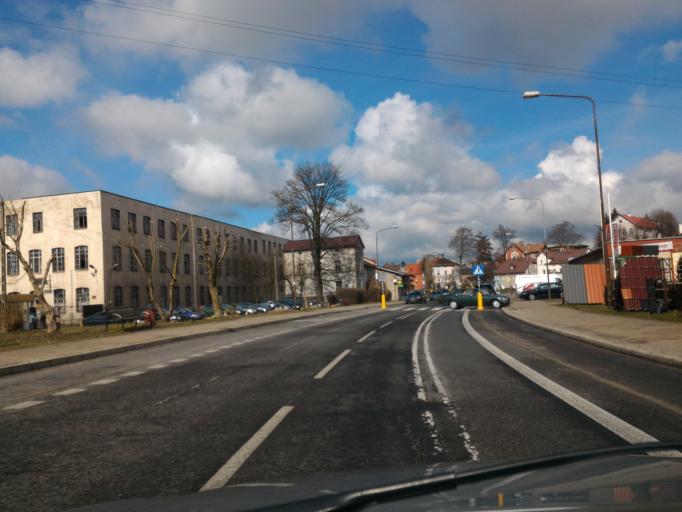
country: PL
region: Silesian Voivodeship
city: Zawidow
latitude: 51.0237
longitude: 15.0626
